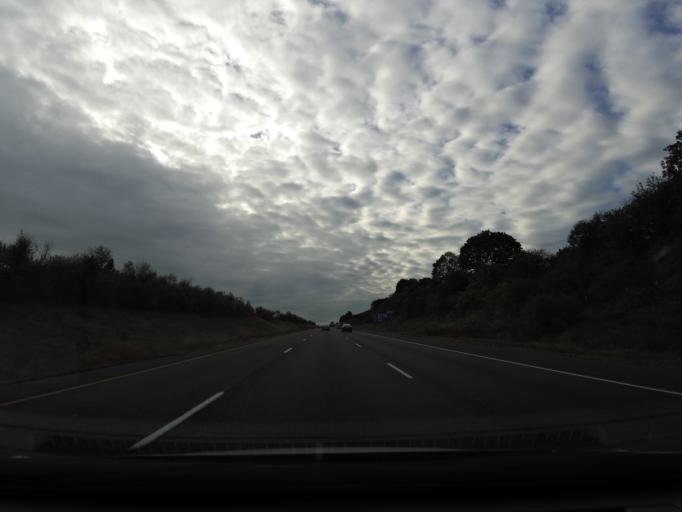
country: CA
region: Ontario
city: Cobourg
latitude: 43.9688
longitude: -78.3023
